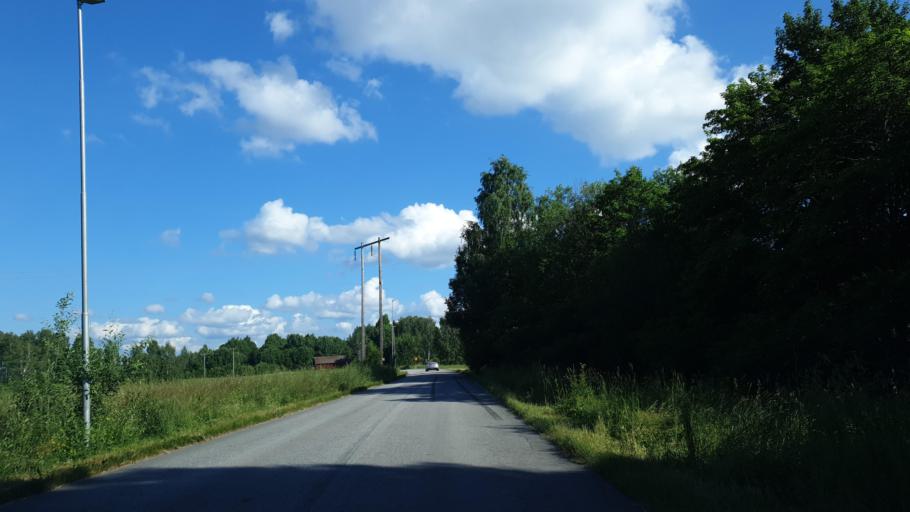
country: SE
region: Dalarna
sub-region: Avesta Kommun
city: Avesta
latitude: 60.1278
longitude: 16.2667
